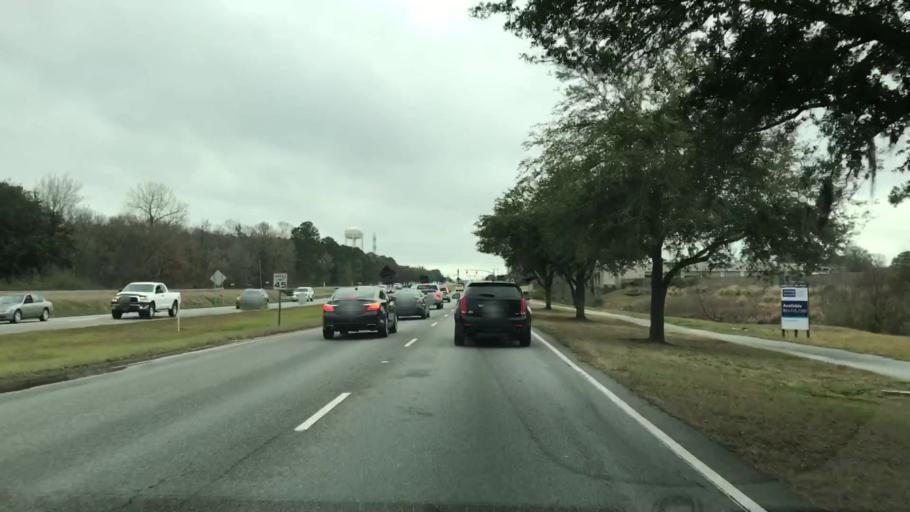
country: US
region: South Carolina
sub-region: Berkeley County
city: Goose Creek
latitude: 33.0100
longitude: -80.0372
